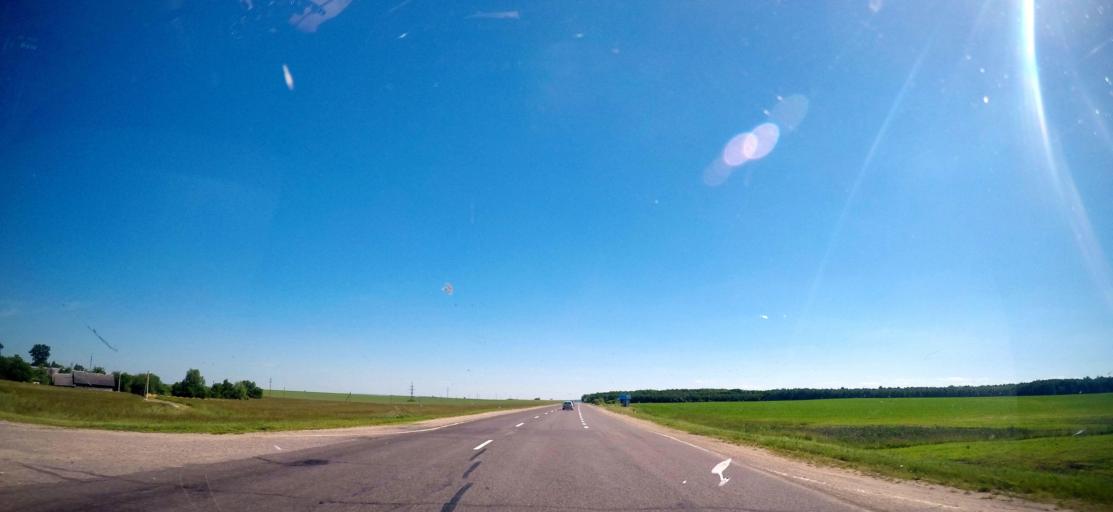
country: BY
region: Grodnenskaya
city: Indura
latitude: 53.5044
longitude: 23.8791
